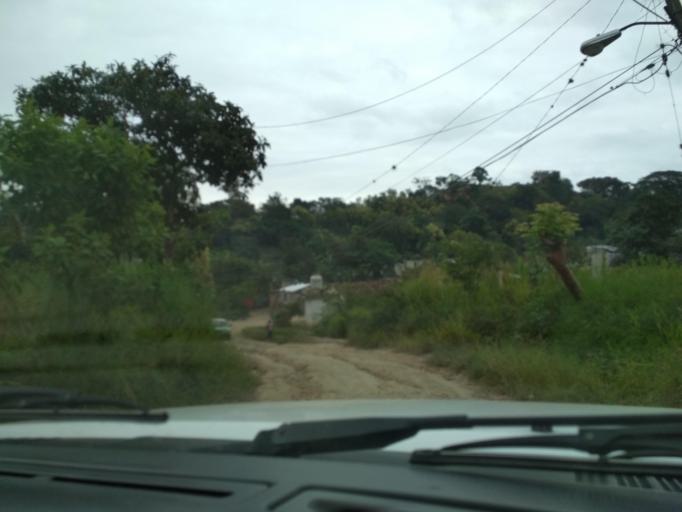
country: MX
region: Veracruz
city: El Castillo
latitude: 19.5793
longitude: -96.8662
